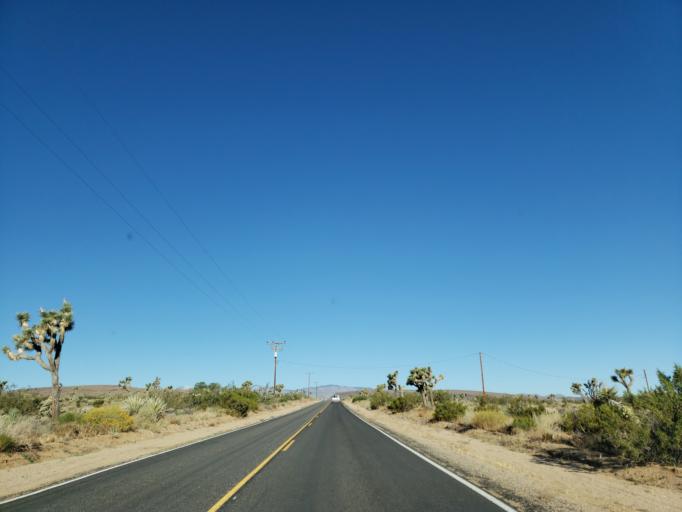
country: US
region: California
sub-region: San Bernardino County
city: Yucca Valley
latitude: 34.1935
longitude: -116.4072
